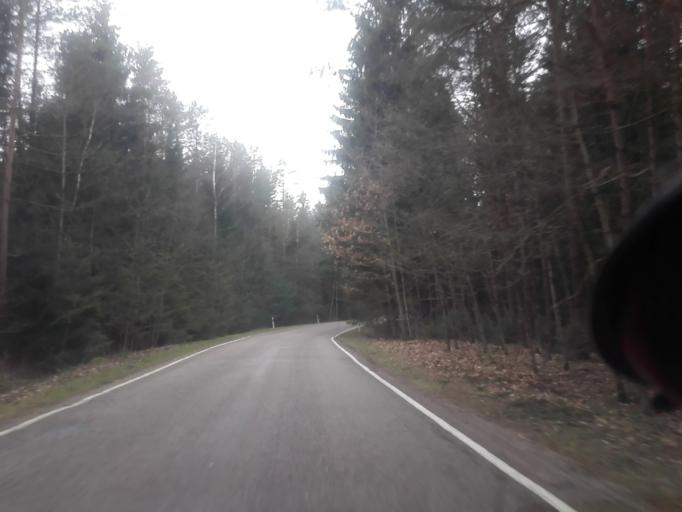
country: PL
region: Podlasie
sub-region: Powiat sejnenski
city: Krasnopol
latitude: 54.1616
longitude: 23.2334
